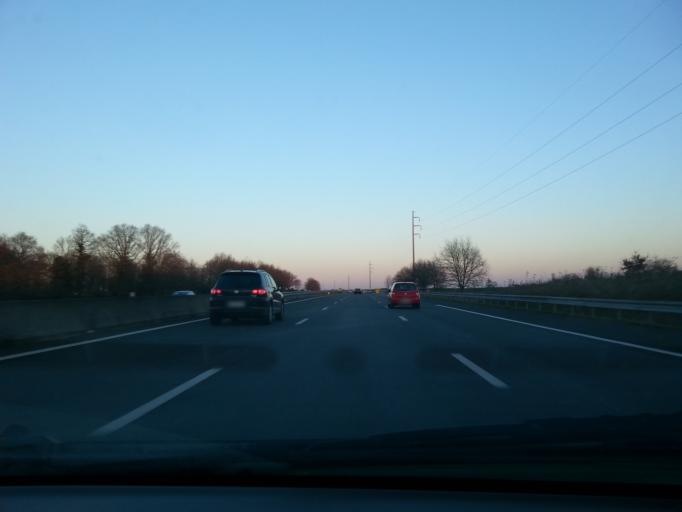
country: FR
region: Centre
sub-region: Departement d'Eure-et-Loir
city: Yevres
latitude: 48.2857
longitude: 1.2507
